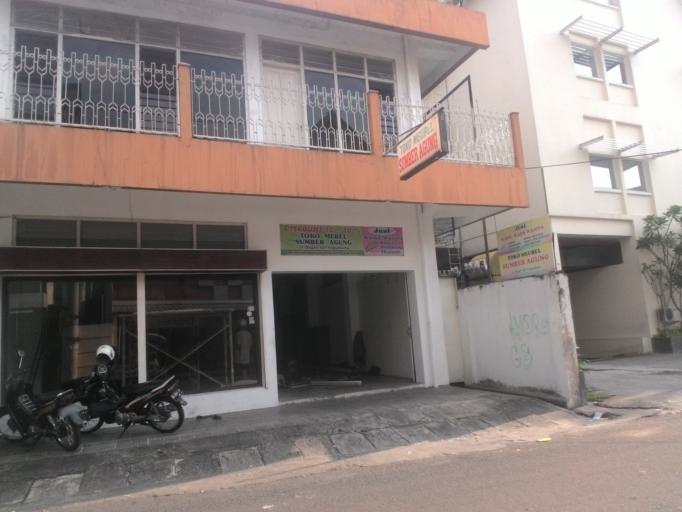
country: ID
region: Daerah Istimewa Yogyakarta
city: Yogyakarta
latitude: -7.7935
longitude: 110.3618
